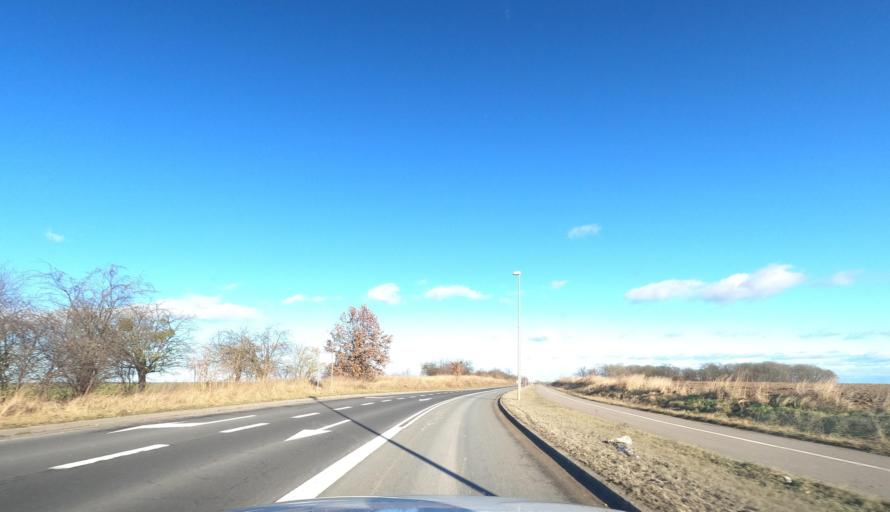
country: PL
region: West Pomeranian Voivodeship
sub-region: Powiat pyrzycki
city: Warnice
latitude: 53.2958
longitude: 14.9592
